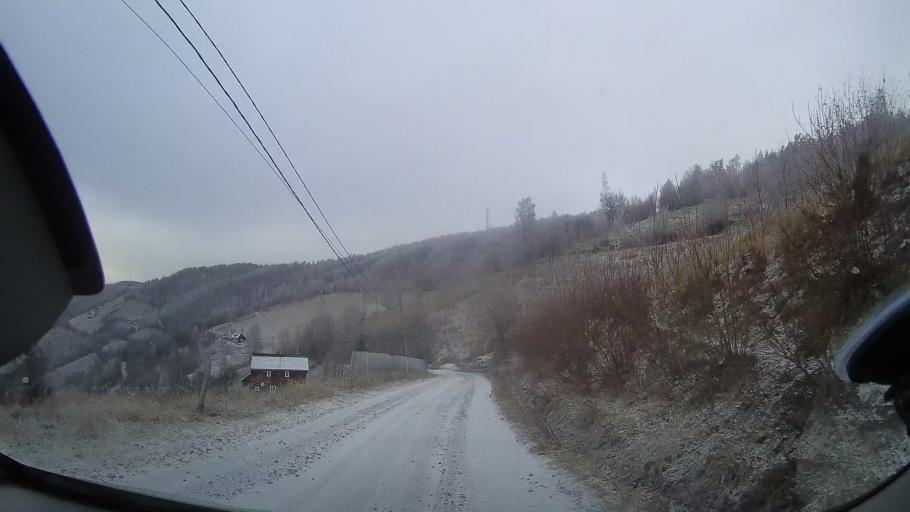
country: RO
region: Cluj
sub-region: Comuna Valea Ierii
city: Valea Ierii
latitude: 46.6651
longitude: 23.3342
